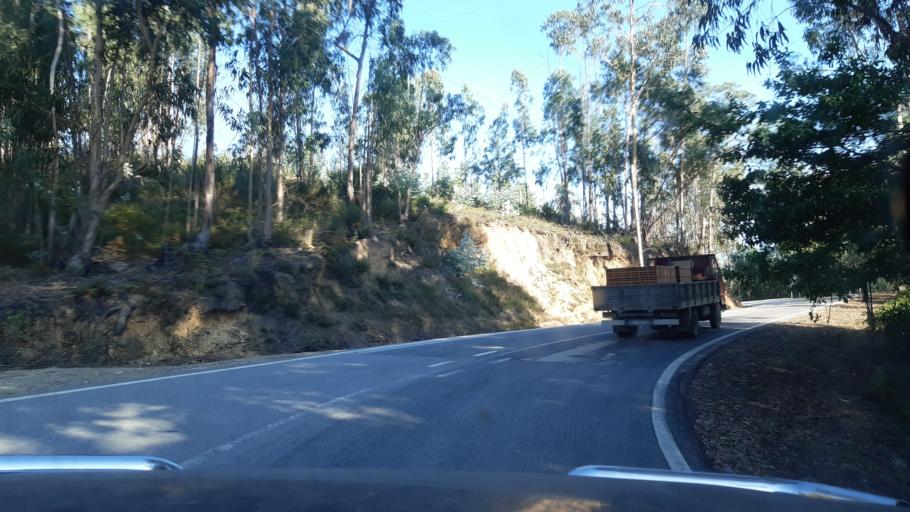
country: PT
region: Aveiro
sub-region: Agueda
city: Agueda
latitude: 40.5644
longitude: -8.3917
